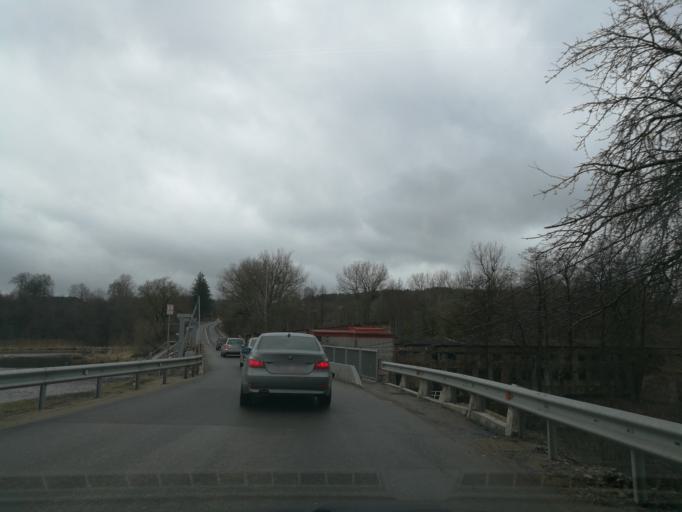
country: LT
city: Grigiskes
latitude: 54.6480
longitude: 25.1206
